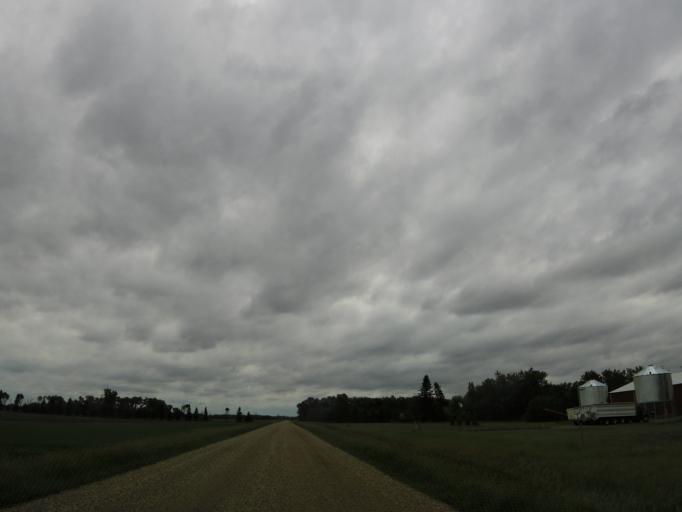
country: US
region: North Dakota
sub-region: Walsh County
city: Grafton
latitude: 48.4695
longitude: -97.5134
